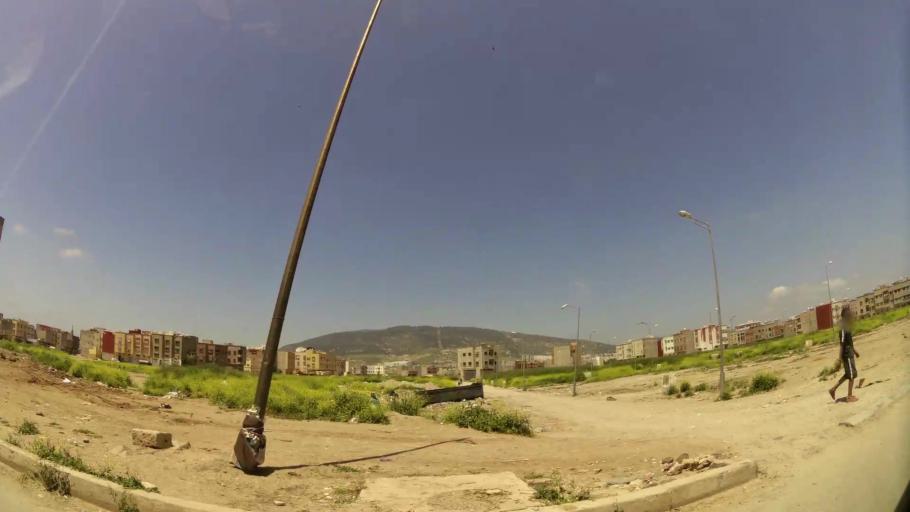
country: MA
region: Fes-Boulemane
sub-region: Fes
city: Fes
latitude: 34.0334
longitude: -5.0459
